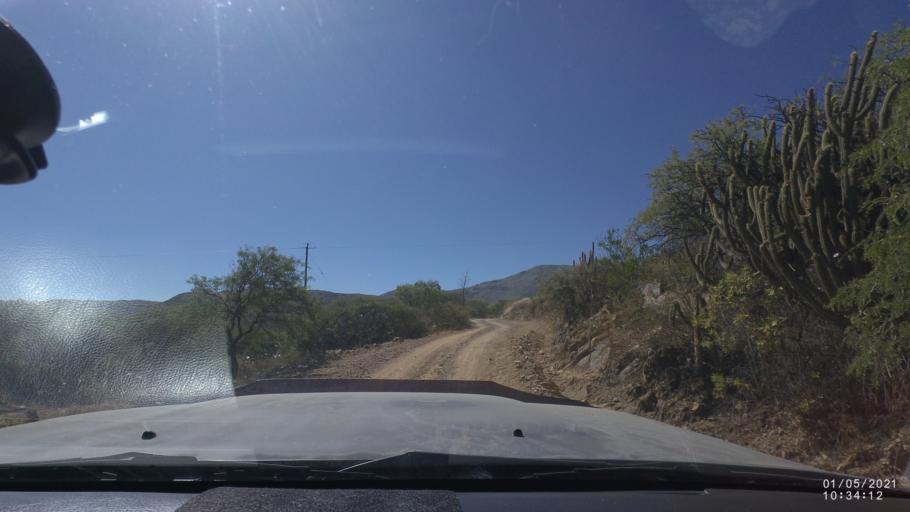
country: BO
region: Cochabamba
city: Capinota
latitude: -17.5971
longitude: -66.1912
